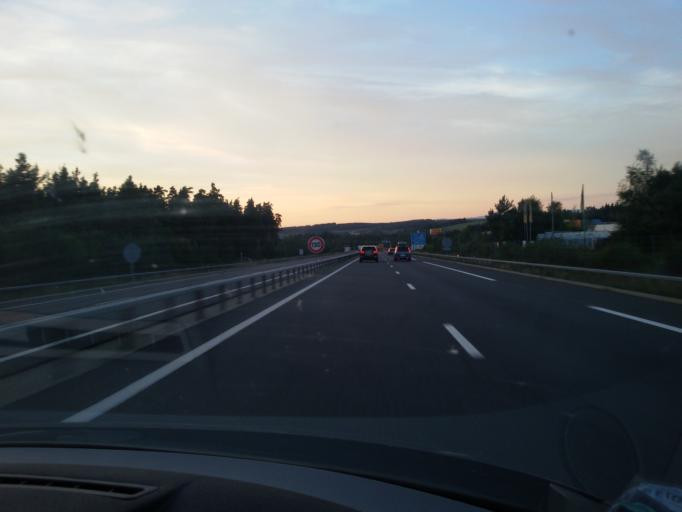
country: FR
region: Languedoc-Roussillon
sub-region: Departement de la Lozere
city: Aumont-Aubrac
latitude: 44.7385
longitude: 3.2890
